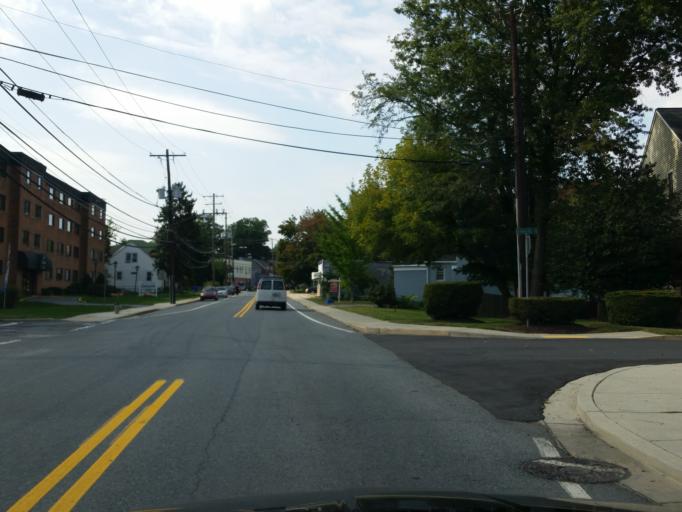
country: US
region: Maryland
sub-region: Montgomery County
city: Silver Spring
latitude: 38.9906
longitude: -77.0171
